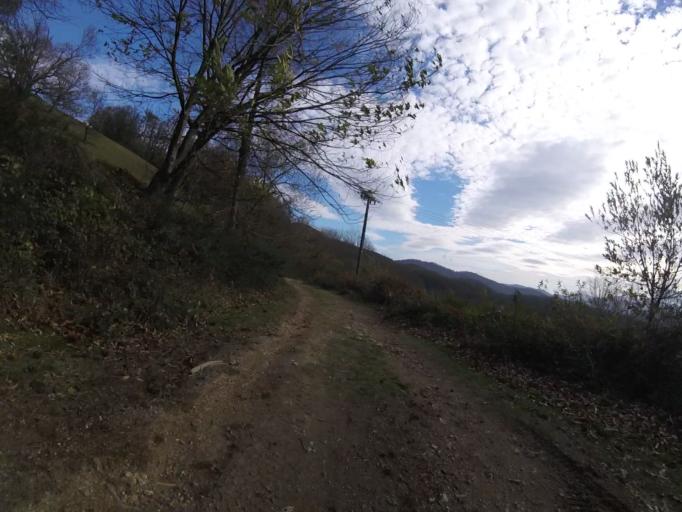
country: ES
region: Navarre
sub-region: Provincia de Navarra
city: Arano
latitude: 43.2403
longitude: -1.8477
